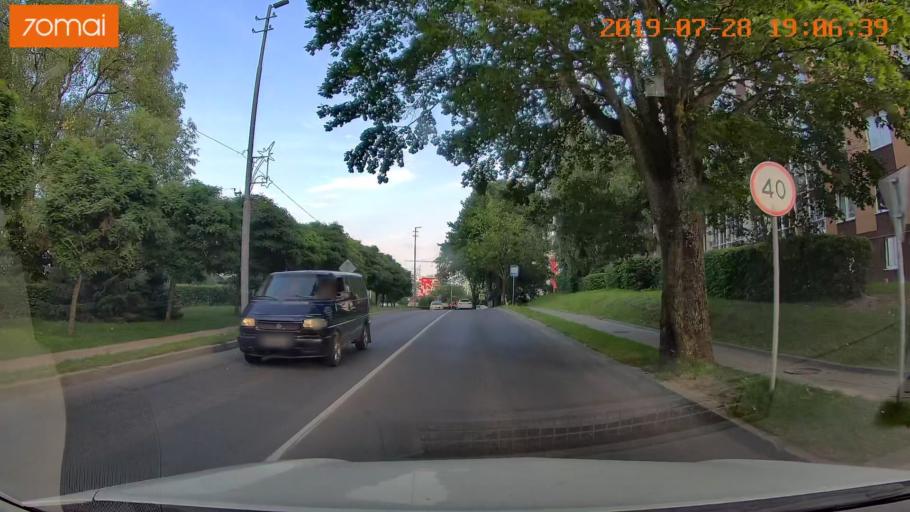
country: RU
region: Kaliningrad
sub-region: Gorod Svetlogorsk
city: Svetlogorsk
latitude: 54.9302
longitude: 20.1666
